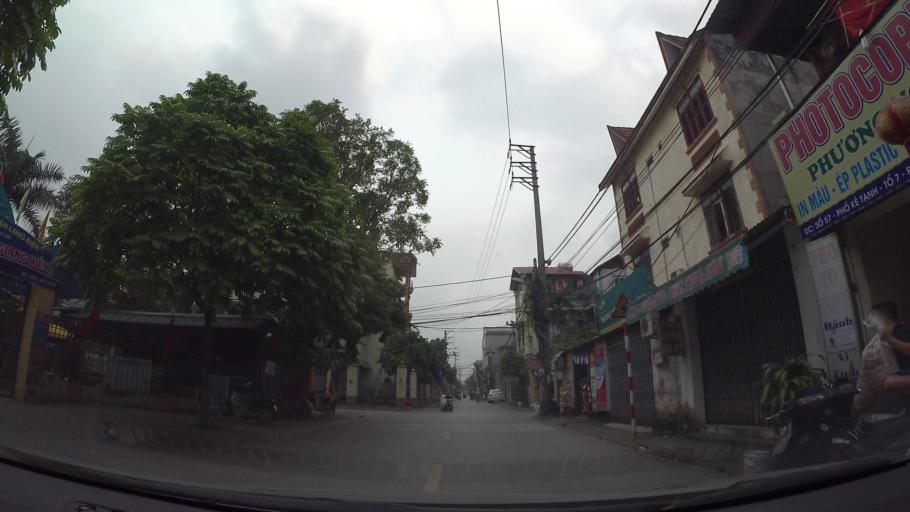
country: VN
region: Ha Noi
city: Trau Quy
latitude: 21.0618
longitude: 105.9173
